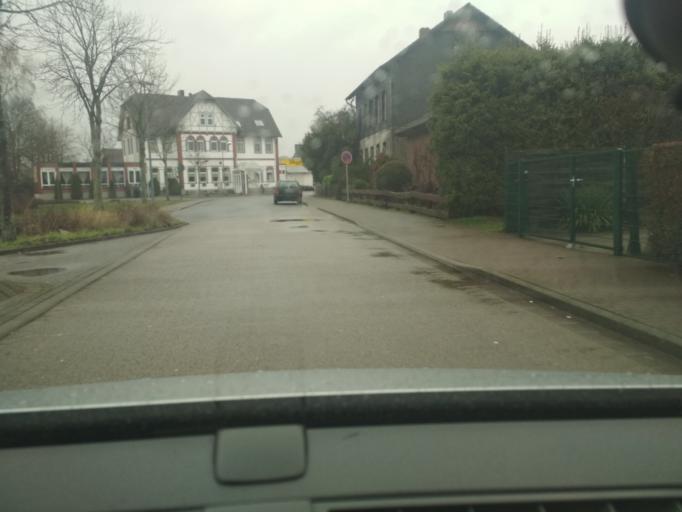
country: DE
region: Lower Saxony
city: Wittingen
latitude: 52.7284
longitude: 10.7246
